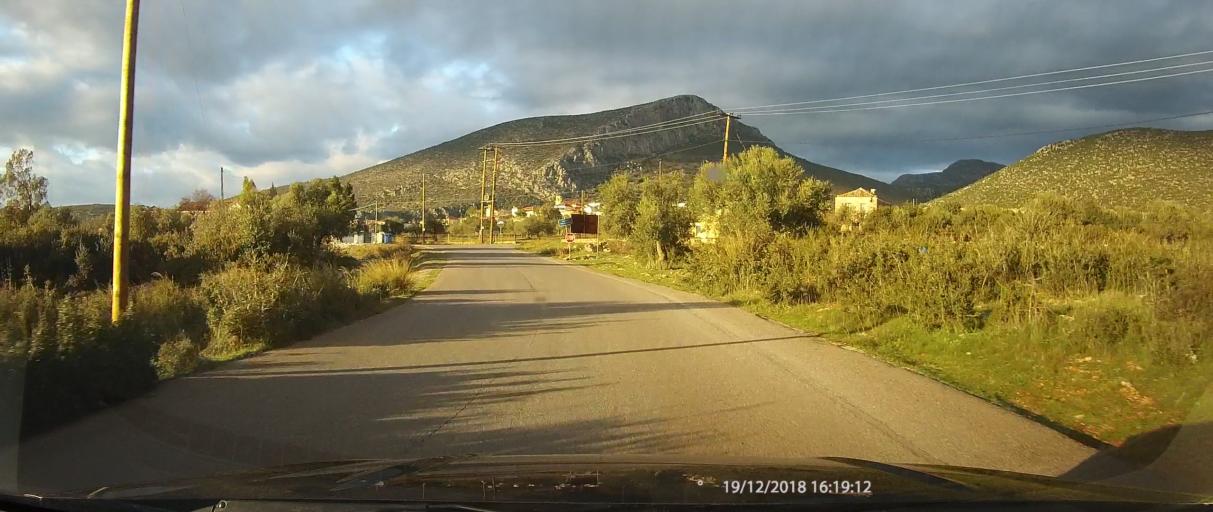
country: GR
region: Peloponnese
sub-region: Nomos Lakonias
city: Kato Glikovrisi
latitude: 36.9306
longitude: 22.8228
